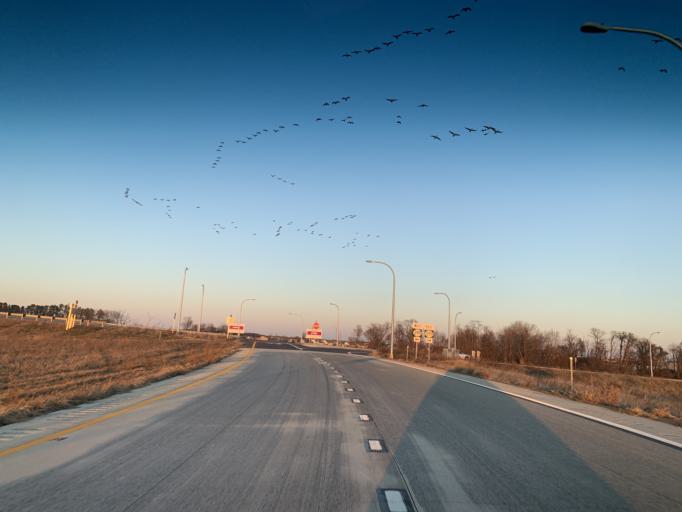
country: US
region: Delaware
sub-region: New Castle County
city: Middletown
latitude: 39.4436
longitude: -75.7513
